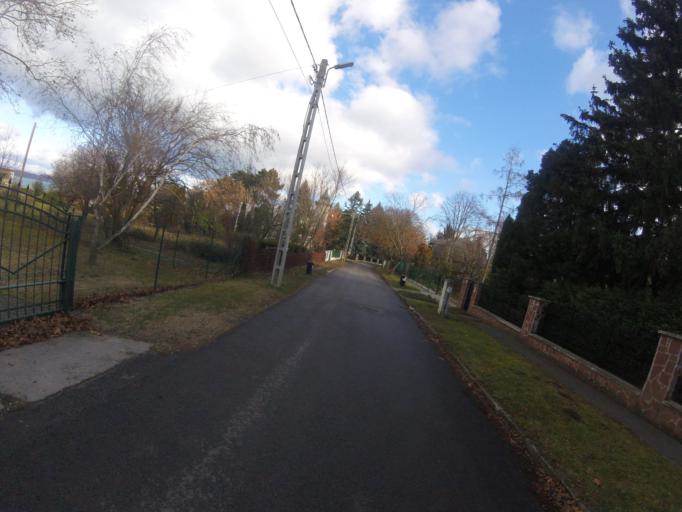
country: HU
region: Somogy
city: Balatonfoldvar
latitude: 46.8474
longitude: 17.8712
